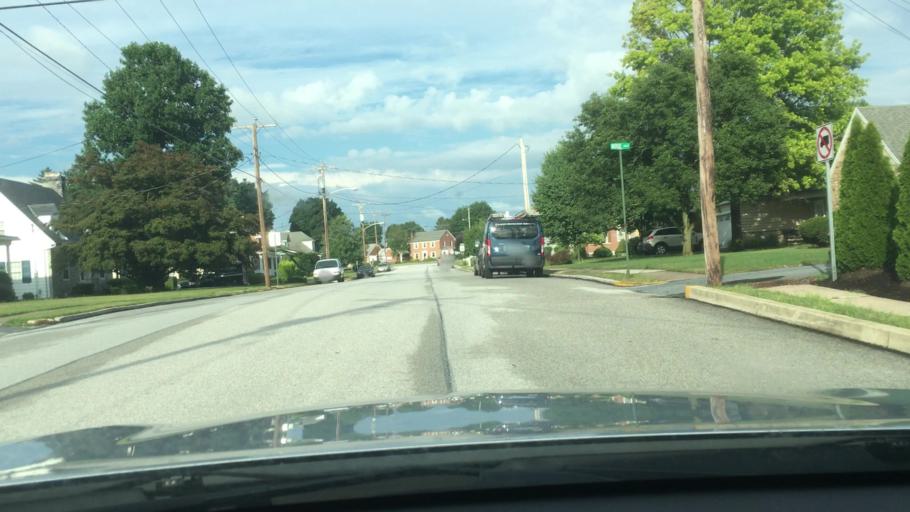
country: US
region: Pennsylvania
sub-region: York County
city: Dillsburg
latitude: 40.1133
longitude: -77.0353
